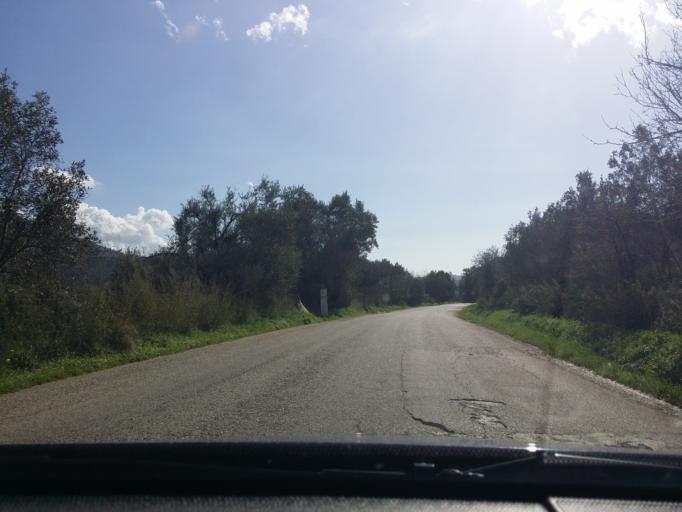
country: GR
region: West Greece
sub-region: Nomos Aitolias kai Akarnanias
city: Astakos
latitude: 38.5590
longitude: 21.0972
